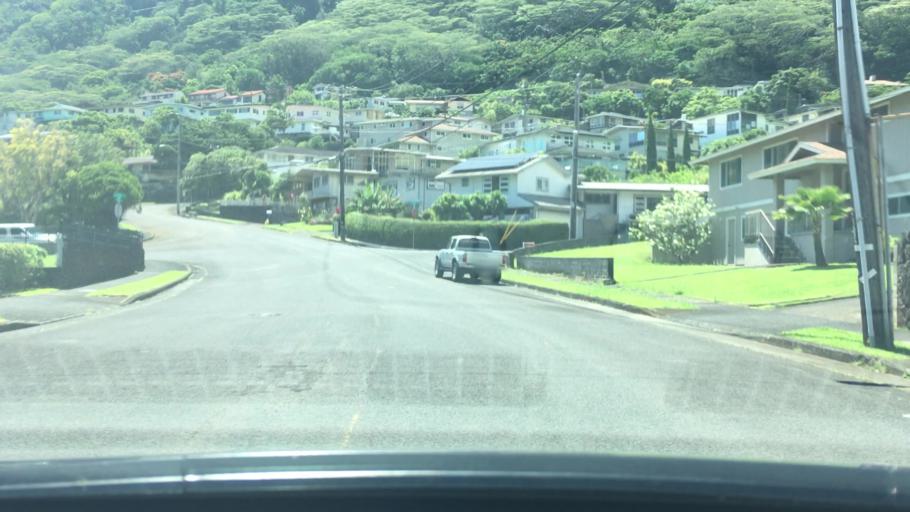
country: US
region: Hawaii
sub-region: Honolulu County
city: Honolulu
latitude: 21.3237
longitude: -157.8038
